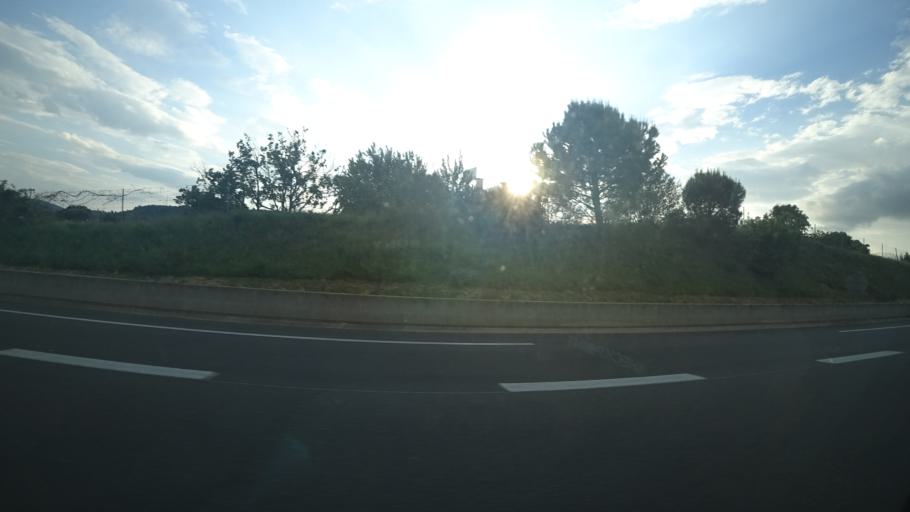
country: FR
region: Languedoc-Roussillon
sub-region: Departement de l'Herault
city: Nebian
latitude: 43.6492
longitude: 3.4497
